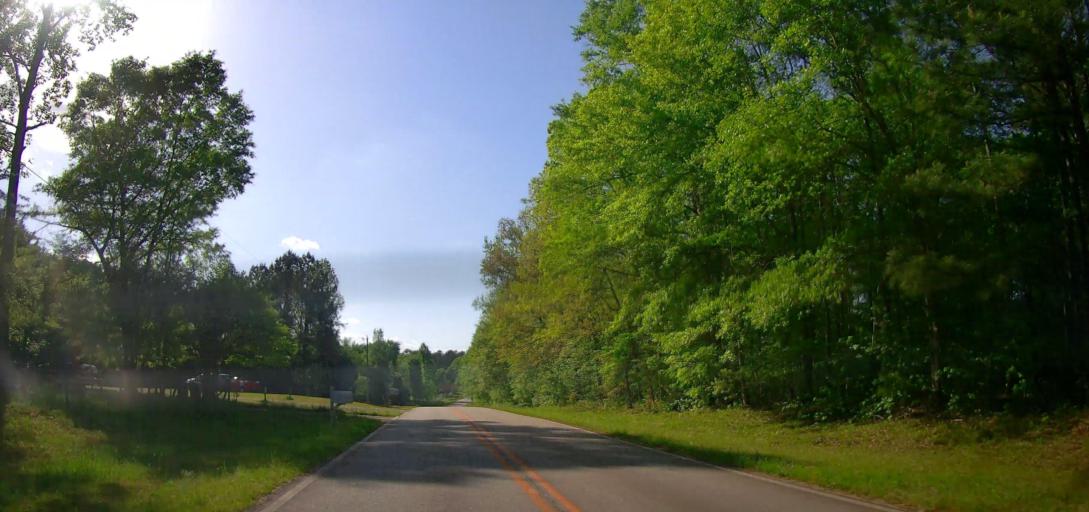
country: US
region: Georgia
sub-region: Morgan County
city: Madison
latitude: 33.5155
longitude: -83.4993
